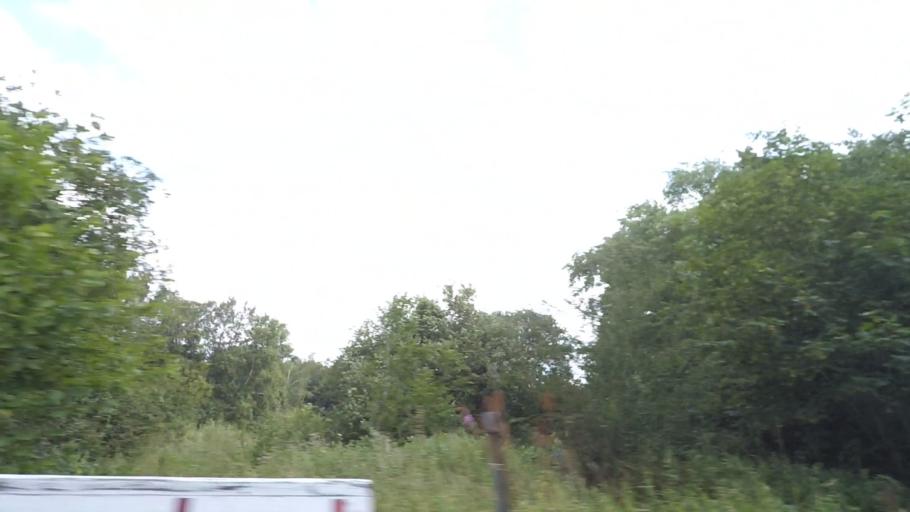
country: DK
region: Central Jutland
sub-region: Syddjurs Kommune
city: Ryomgard
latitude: 56.4796
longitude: 10.4860
